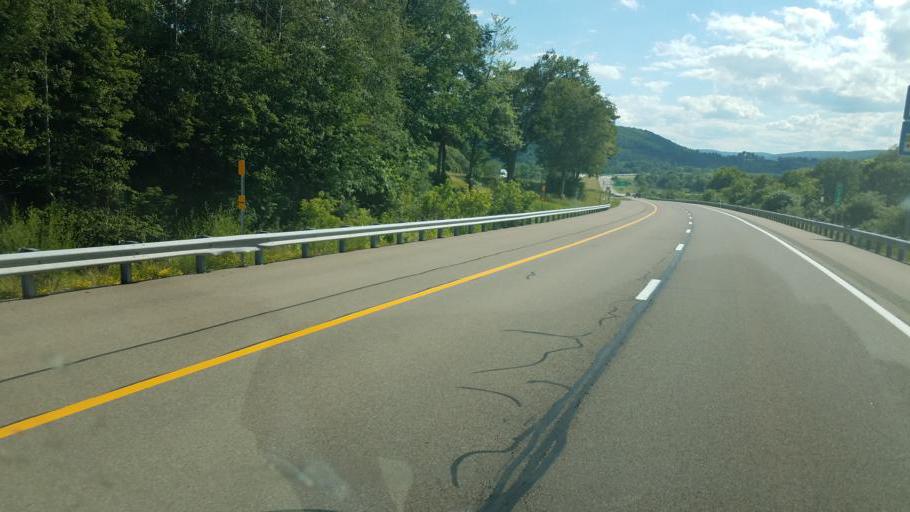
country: US
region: New York
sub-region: Steuben County
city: Hornell
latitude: 42.3779
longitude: -77.6685
